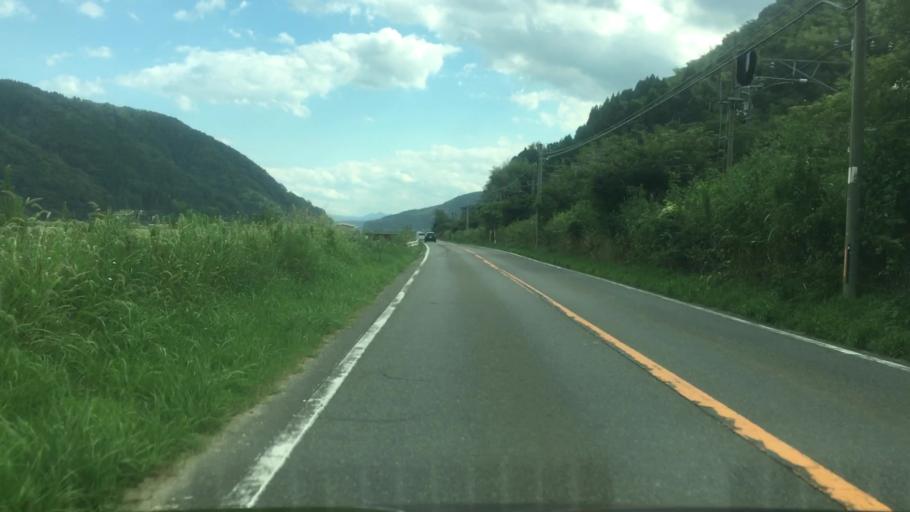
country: JP
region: Hyogo
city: Toyooka
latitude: 35.6020
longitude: 134.8017
